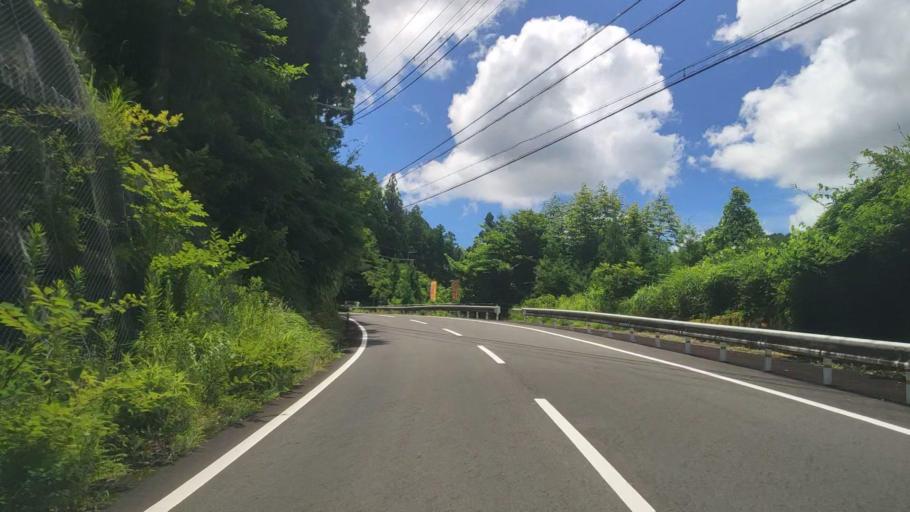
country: JP
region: Mie
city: Owase
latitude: 33.9540
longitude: 136.0688
